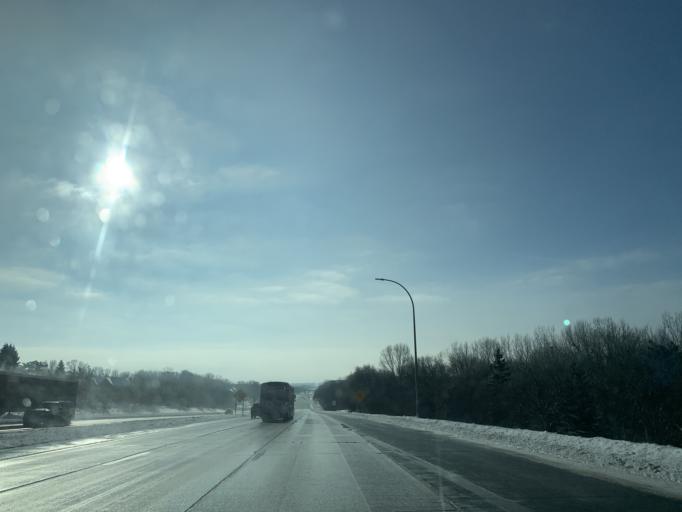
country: US
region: Minnesota
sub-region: Dakota County
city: Apple Valley
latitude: 44.7547
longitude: -93.2180
